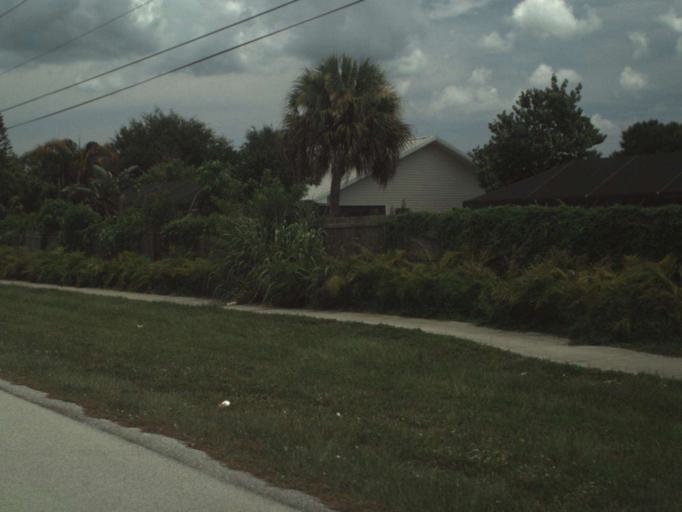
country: US
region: Florida
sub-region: Saint Lucie County
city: Lakewood Park
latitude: 27.5352
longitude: -80.3859
